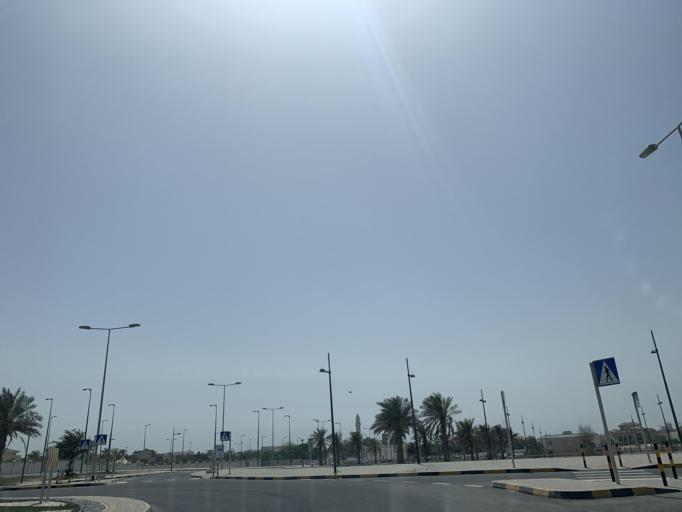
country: BH
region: Northern
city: Madinat `Isa
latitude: 26.1521
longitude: 50.5447
